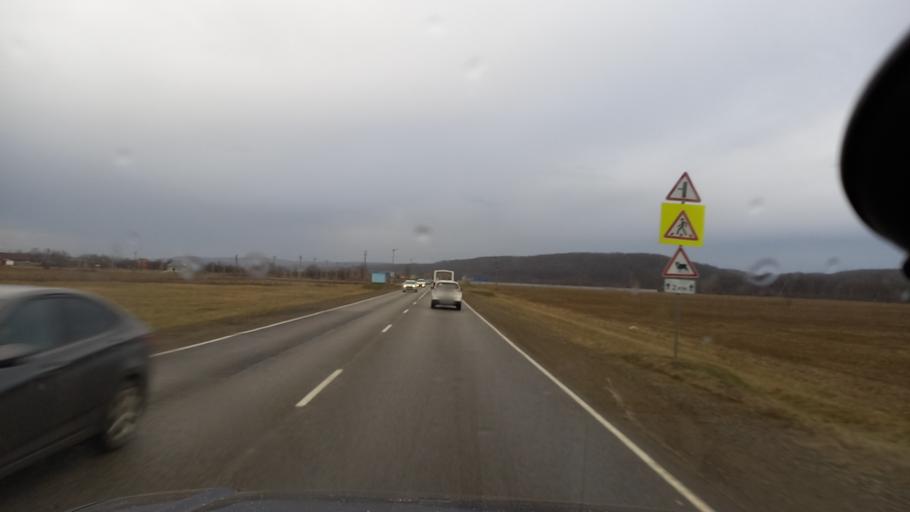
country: RU
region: Adygeya
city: Tul'skiy
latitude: 44.5337
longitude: 40.1388
